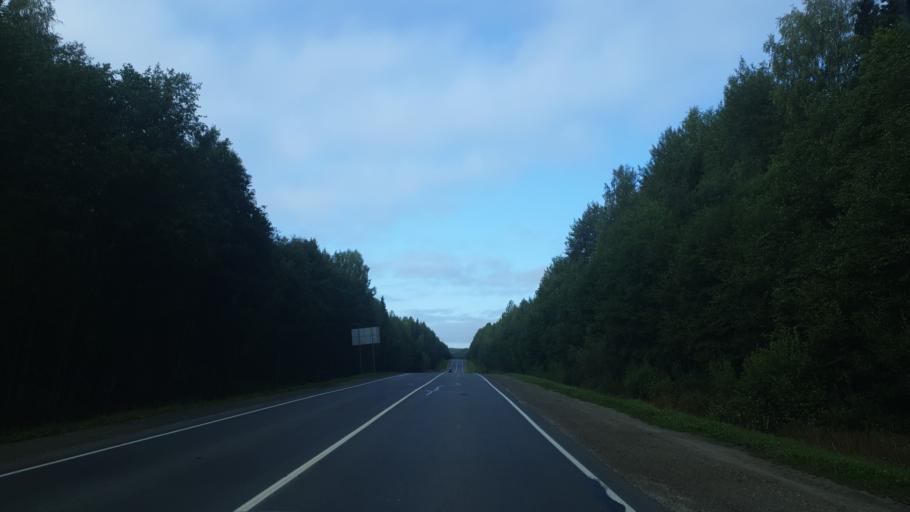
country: RU
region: Komi Republic
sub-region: Syktyvdinskiy Rayon
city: Syktyvkar
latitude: 61.5557
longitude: 50.6298
